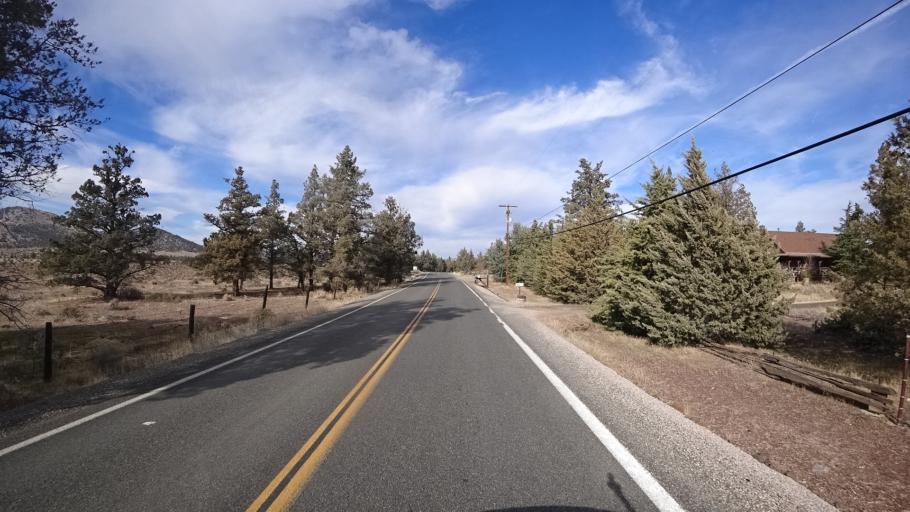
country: US
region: California
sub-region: Siskiyou County
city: Montague
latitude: 41.6532
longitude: -122.3994
